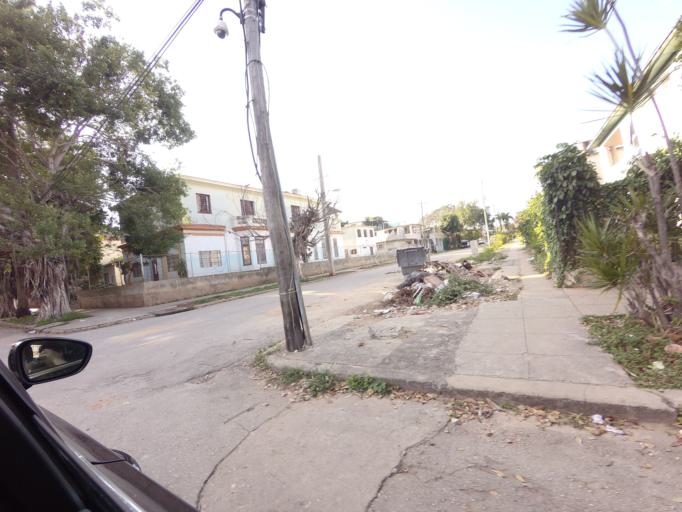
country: CU
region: La Habana
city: Havana
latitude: 23.1138
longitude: -82.4197
